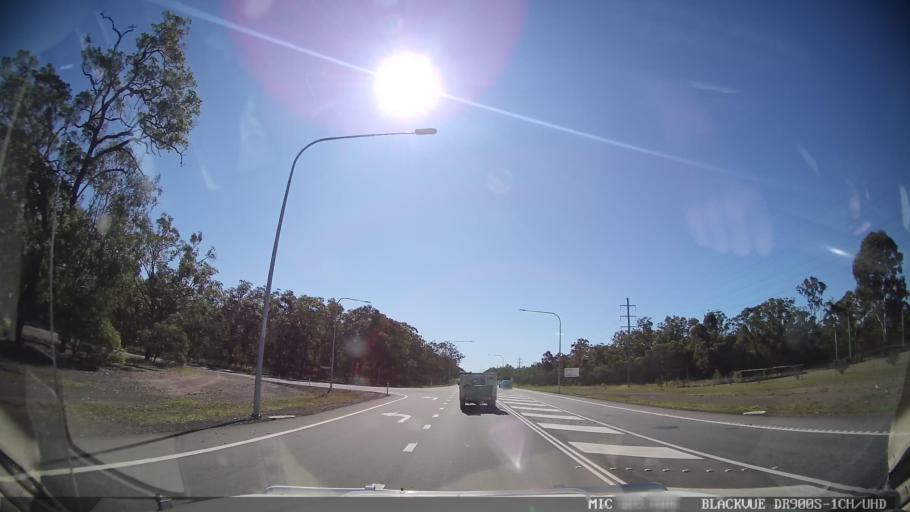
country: AU
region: Queensland
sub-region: Fraser Coast
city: Maryborough
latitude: -25.5115
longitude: 152.6706
